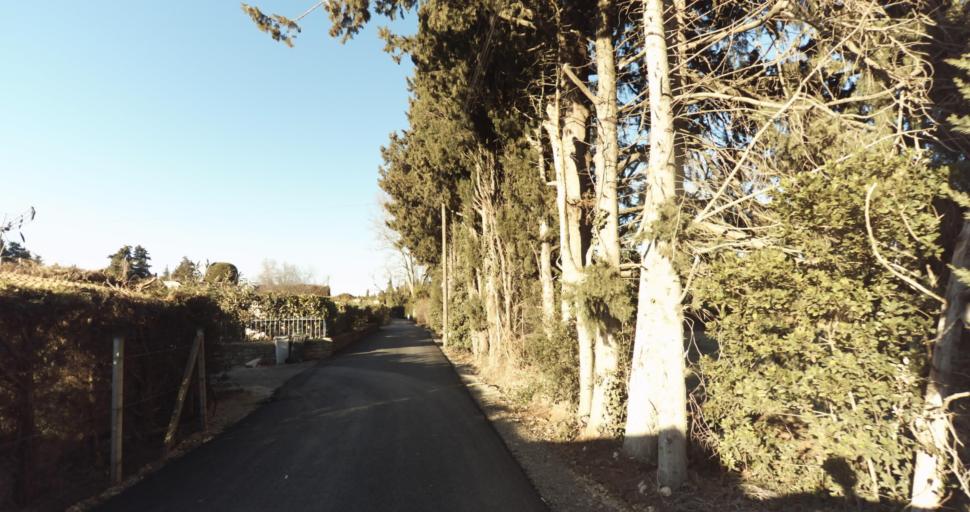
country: FR
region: Provence-Alpes-Cote d'Azur
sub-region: Departement des Bouches-du-Rhone
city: Barbentane
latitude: 43.9048
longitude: 4.7441
